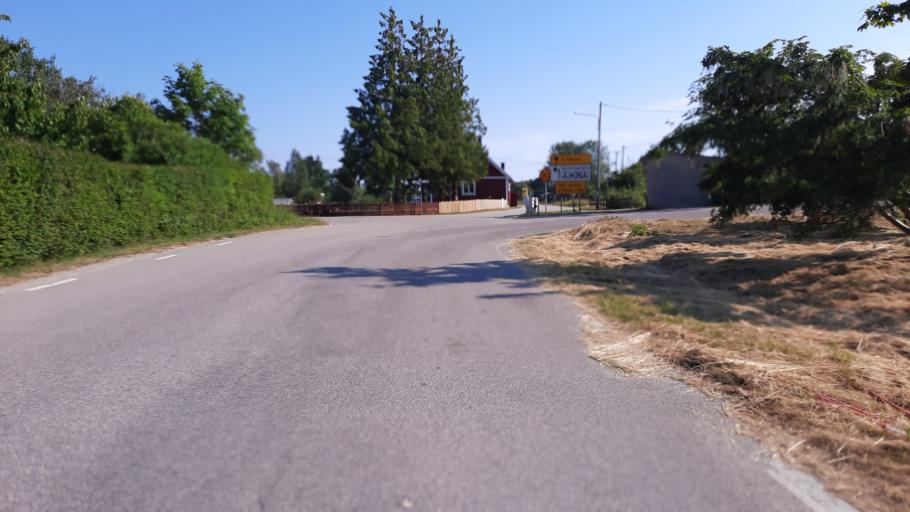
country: SE
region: Blekinge
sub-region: Karlskrona Kommun
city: Sturko
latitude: 56.0880
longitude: 15.6952
